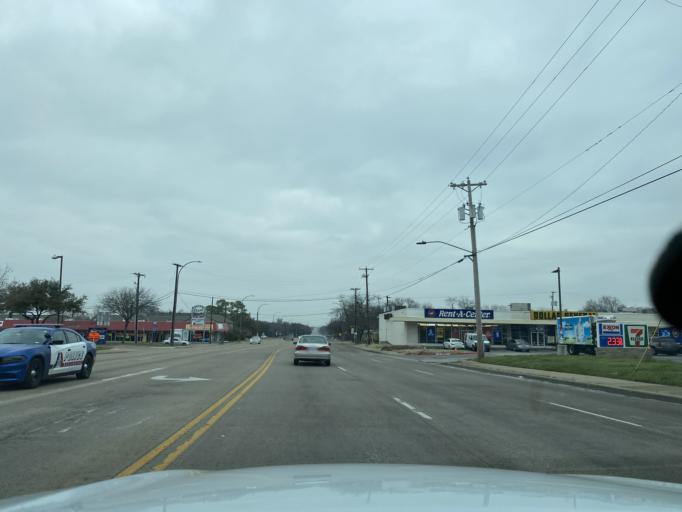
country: US
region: Texas
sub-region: Tarrant County
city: Arlington
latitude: 32.7213
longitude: -97.0974
